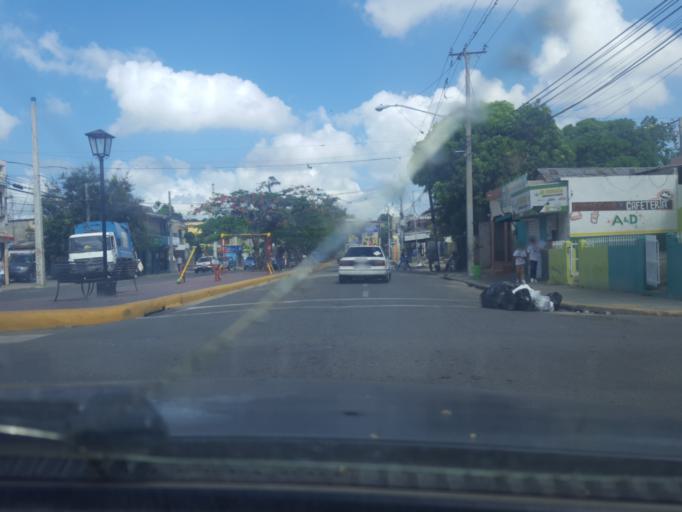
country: DO
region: Santiago
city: Santiago de los Caballeros
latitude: 19.4765
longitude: -70.7076
